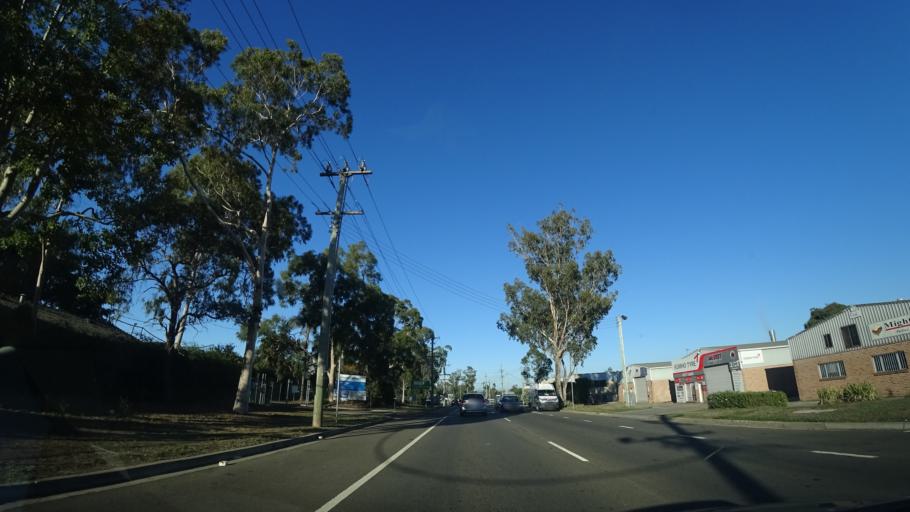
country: AU
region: New South Wales
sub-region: Hawkesbury
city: South Windsor
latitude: -33.6270
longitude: 150.8362
